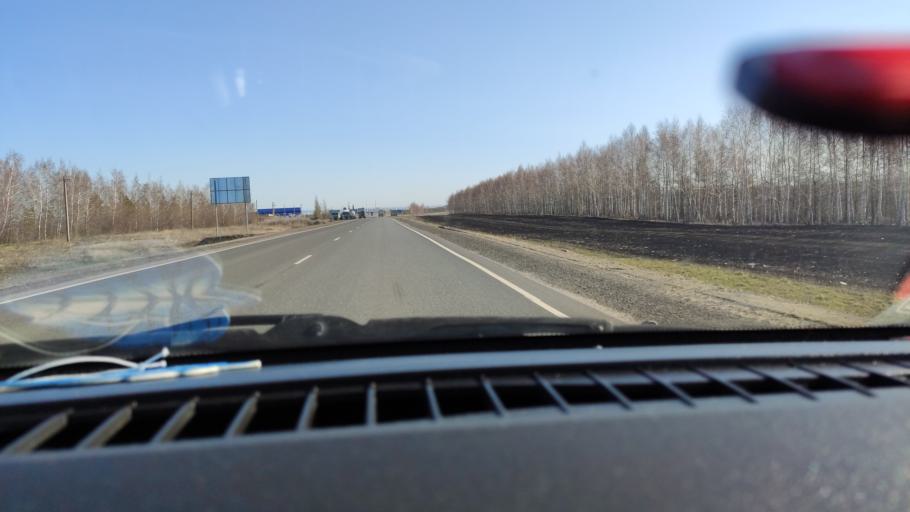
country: RU
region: Samara
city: Syzran'
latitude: 52.9937
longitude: 48.3240
